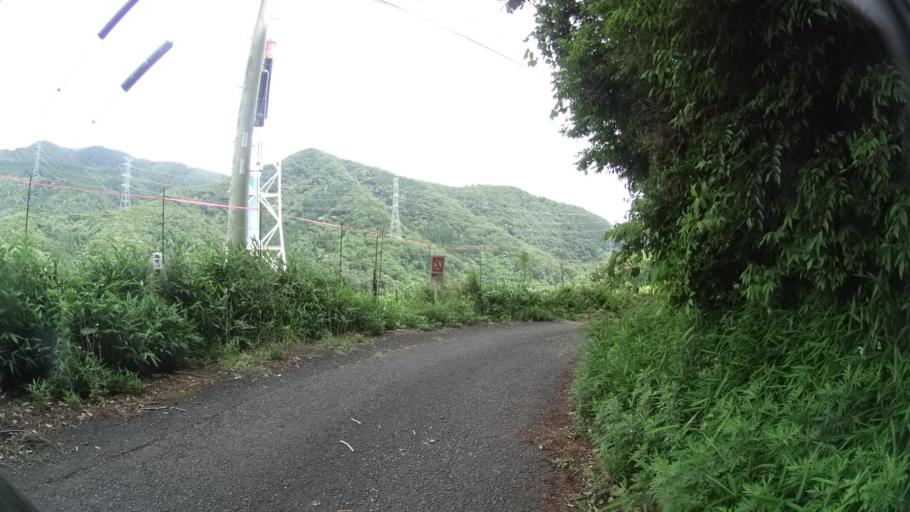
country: JP
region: Kyoto
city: Maizuru
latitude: 35.5329
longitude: 135.3428
